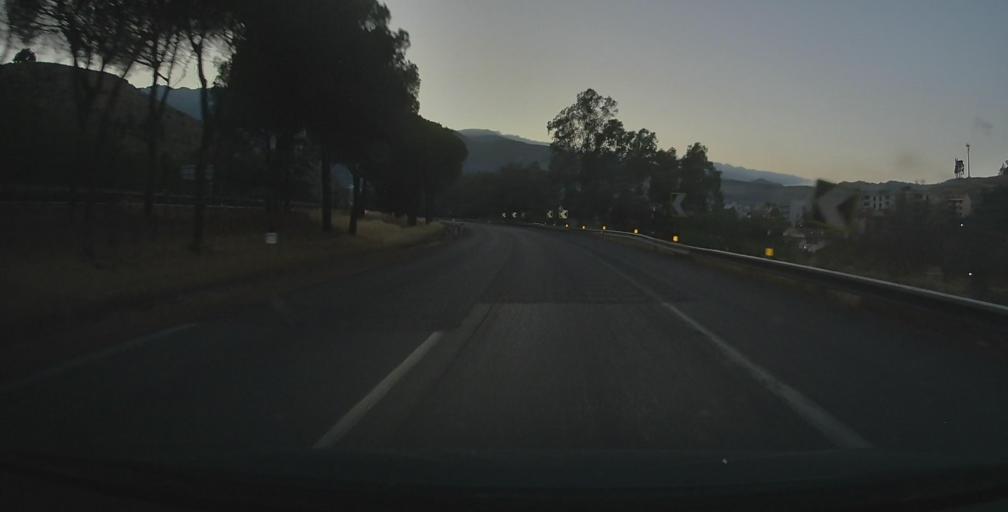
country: IT
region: Sicily
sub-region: Messina
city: Larderia
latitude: 38.1462
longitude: 15.5172
